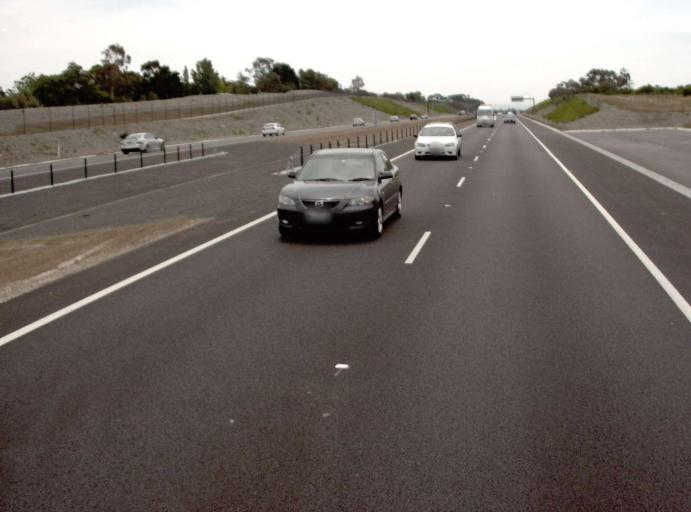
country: AU
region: Victoria
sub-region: Frankston
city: Langwarrin
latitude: -38.1718
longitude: 145.1633
